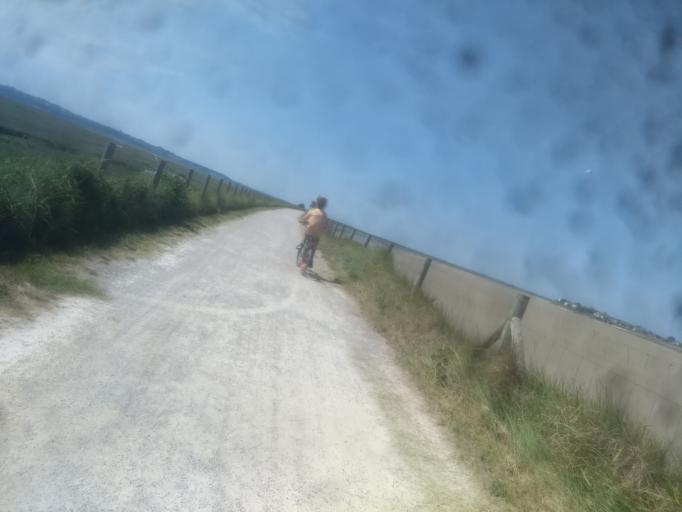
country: FR
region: Picardie
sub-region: Departement de la Somme
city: Le Crotoy
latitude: 50.2151
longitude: 1.6490
